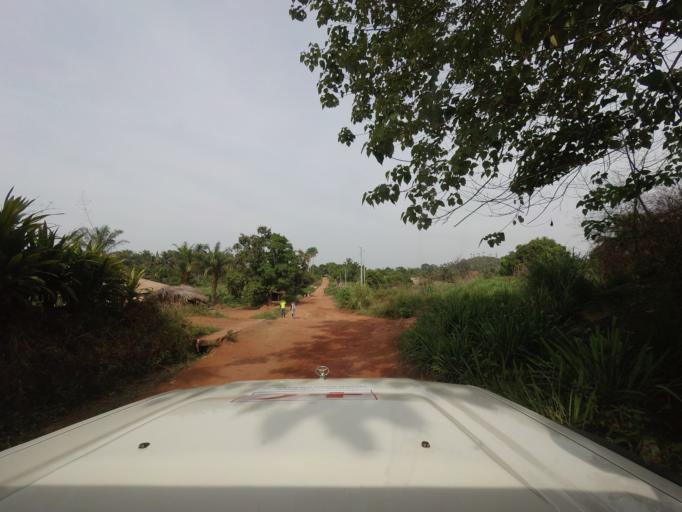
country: GN
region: Nzerekore
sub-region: Macenta
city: Macenta
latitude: 8.5401
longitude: -9.4869
